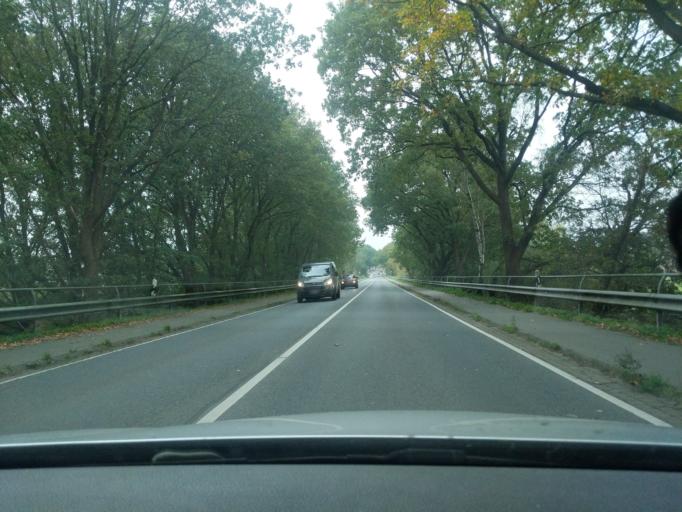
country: DE
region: Lower Saxony
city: Hechthausen
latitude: 53.6390
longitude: 9.2503
